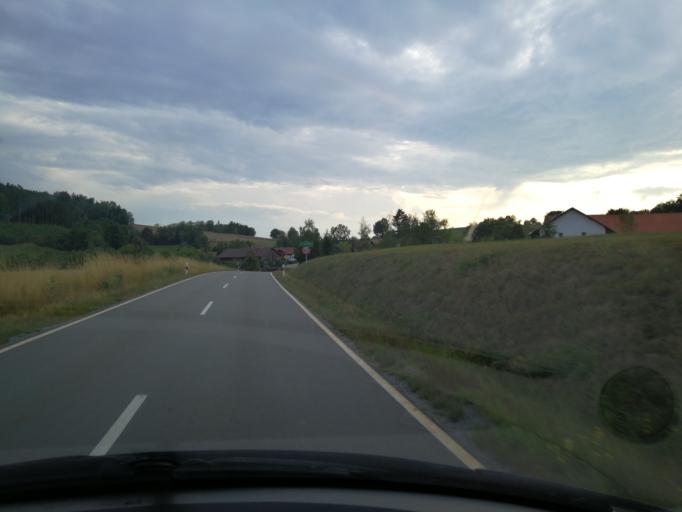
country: DE
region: Bavaria
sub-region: Lower Bavaria
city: Rattiszell
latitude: 49.0366
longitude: 12.6848
